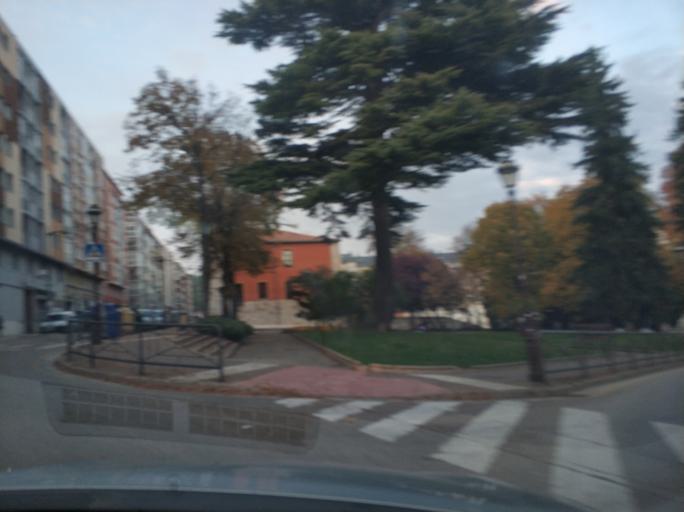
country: ES
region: Castille and Leon
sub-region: Provincia de Burgos
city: Burgos
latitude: 42.3441
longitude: -3.7022
